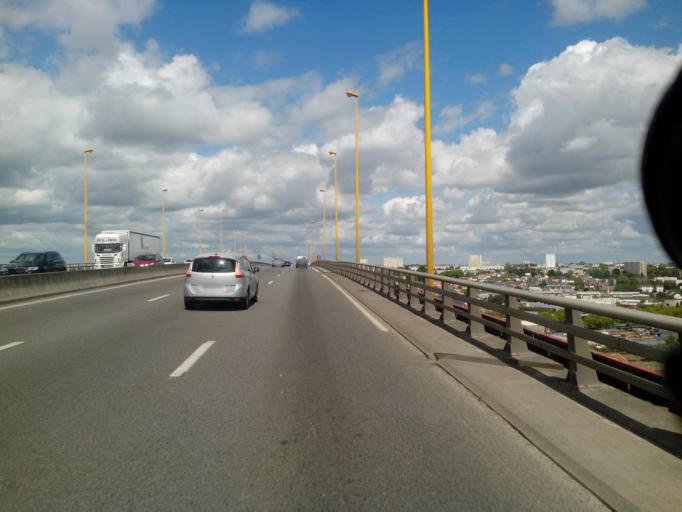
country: FR
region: Pays de la Loire
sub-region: Departement de la Loire-Atlantique
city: Bouguenais
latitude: 47.1917
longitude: -1.6134
